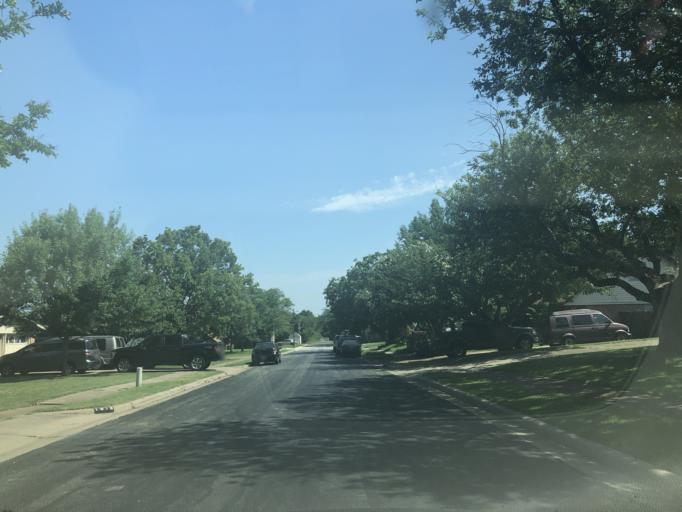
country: US
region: Texas
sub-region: Dallas County
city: Grand Prairie
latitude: 32.7233
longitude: -97.0044
